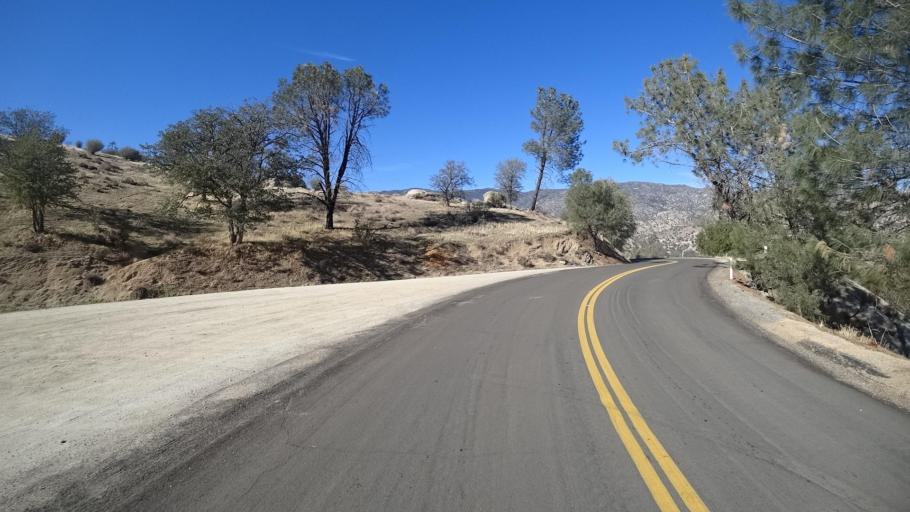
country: US
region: California
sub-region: Kern County
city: Bodfish
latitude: 35.5919
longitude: -118.5163
